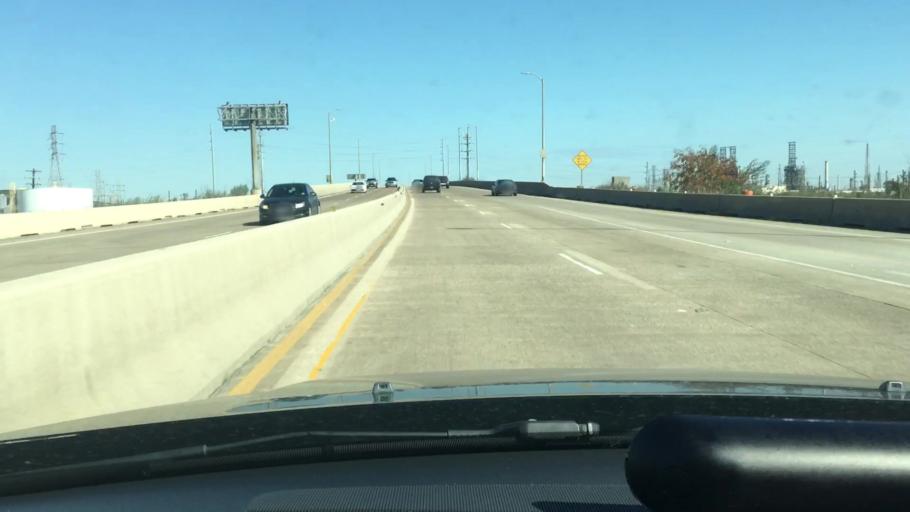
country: US
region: Texas
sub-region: Harris County
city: Deer Park
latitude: 29.7173
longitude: -95.1510
